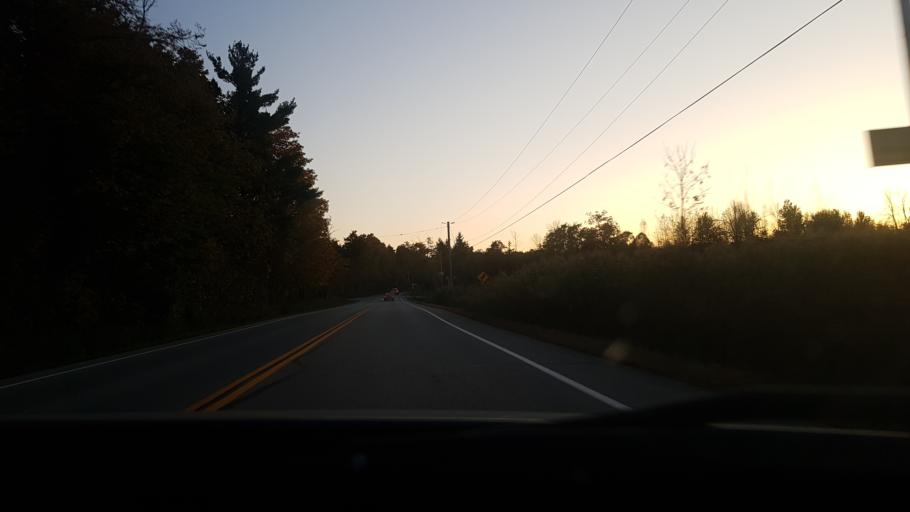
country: CA
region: Ontario
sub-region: Halton
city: Milton
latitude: 43.4576
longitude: -80.0126
